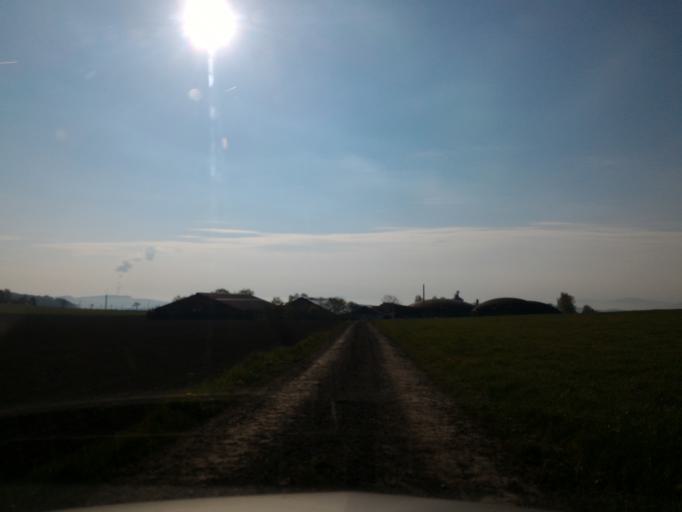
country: DE
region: Saxony
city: Leutersdorf
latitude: 50.9441
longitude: 14.6655
